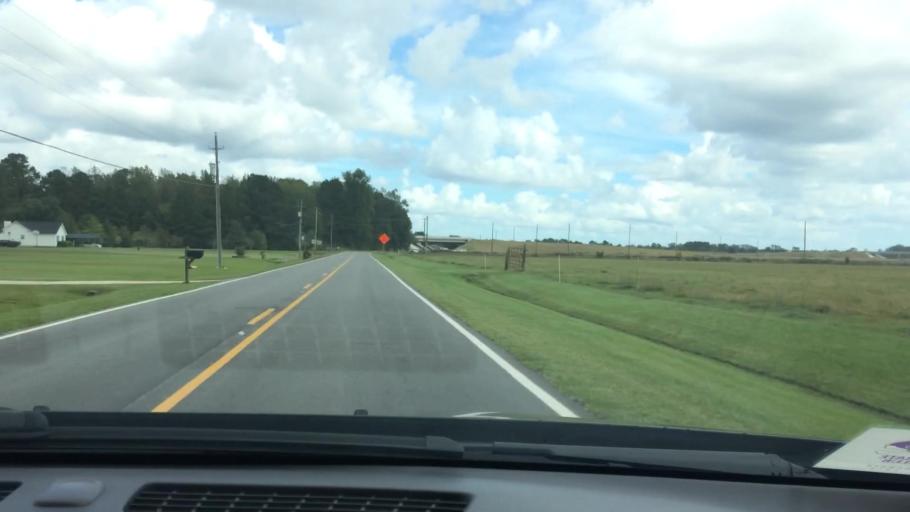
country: US
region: North Carolina
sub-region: Pitt County
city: Ayden
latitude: 35.4667
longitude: -77.4476
